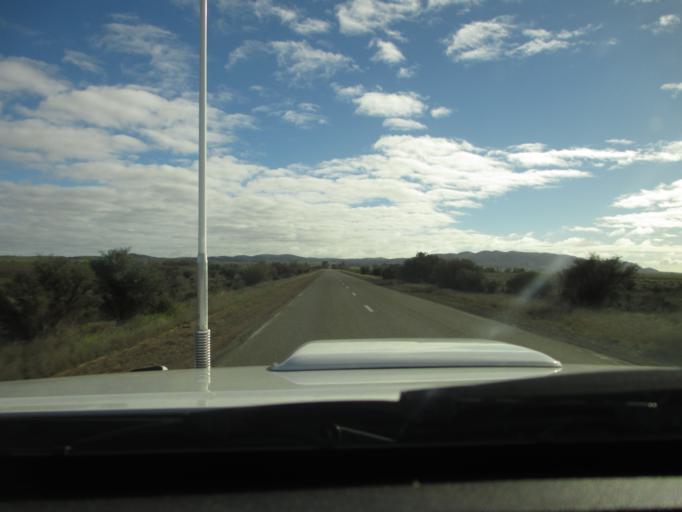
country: AU
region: South Australia
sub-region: Peterborough
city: Peterborough
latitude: -32.6453
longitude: 138.6000
